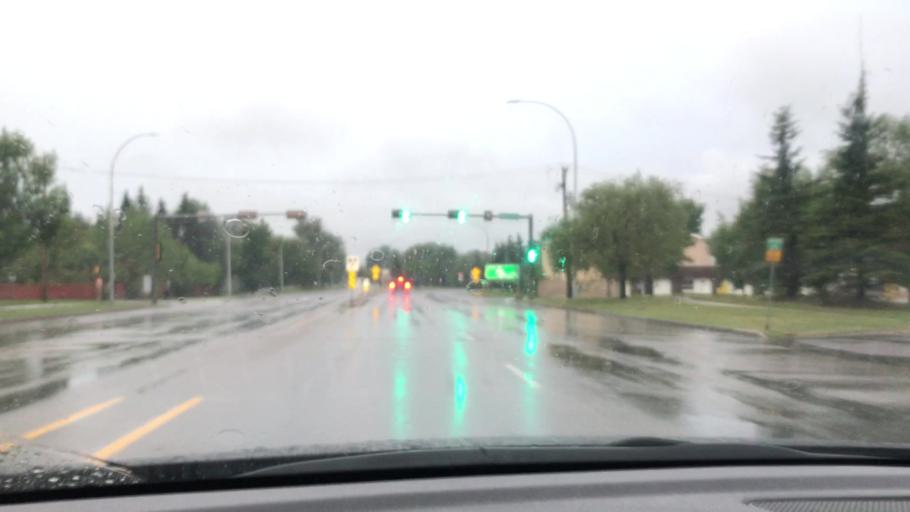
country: CA
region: Alberta
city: Sherwood Park
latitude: 53.5204
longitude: -113.3173
